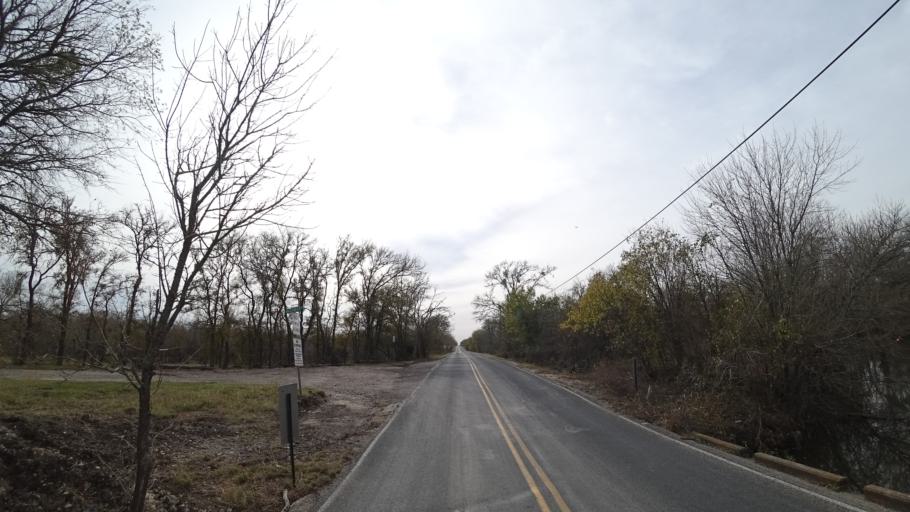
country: US
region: Texas
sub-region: Travis County
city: Garfield
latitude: 30.1338
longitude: -97.5889
